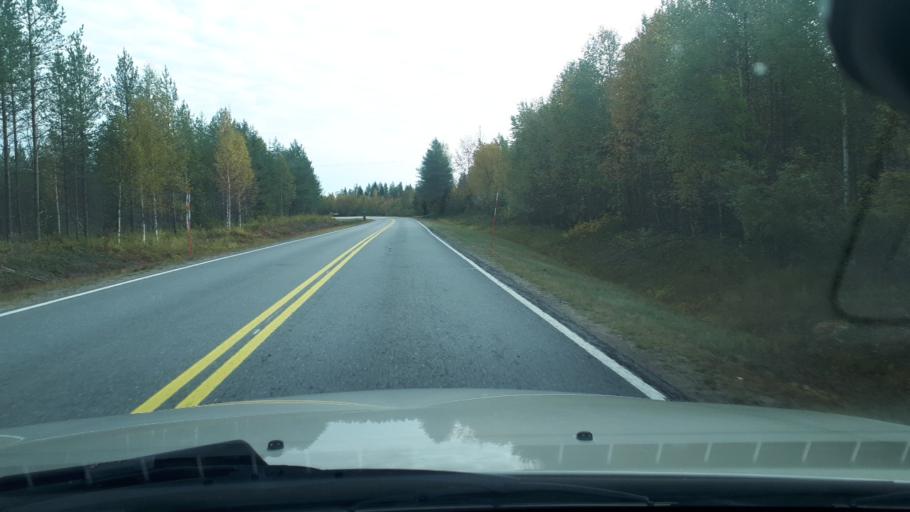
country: FI
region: Lapland
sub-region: Rovaniemi
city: Ranua
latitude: 65.9634
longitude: 25.9685
